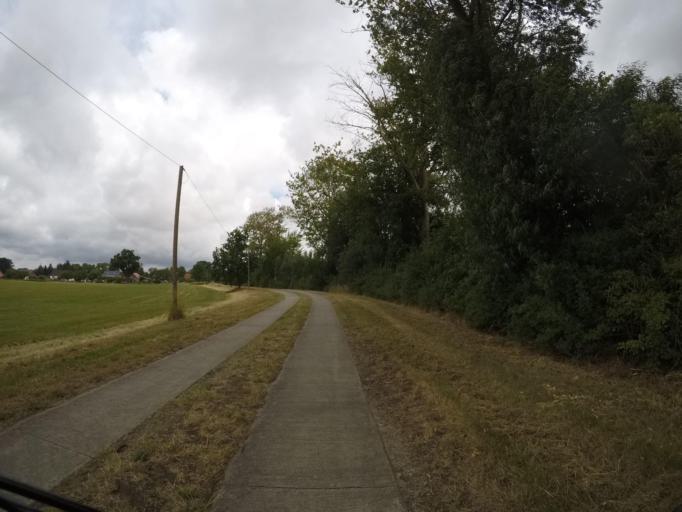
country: DE
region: Lower Saxony
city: Hitzacker
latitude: 53.1795
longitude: 11.1102
